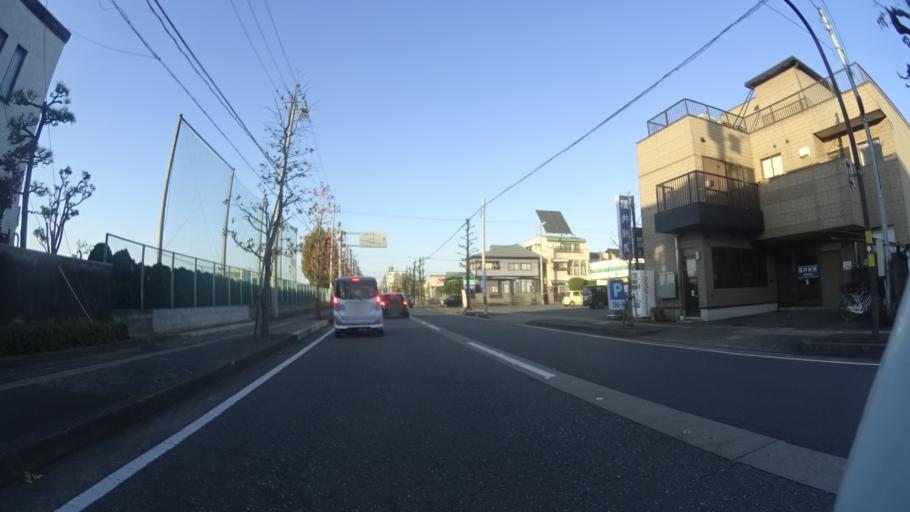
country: JP
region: Fukui
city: Fukui-shi
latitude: 36.0582
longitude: 136.2344
